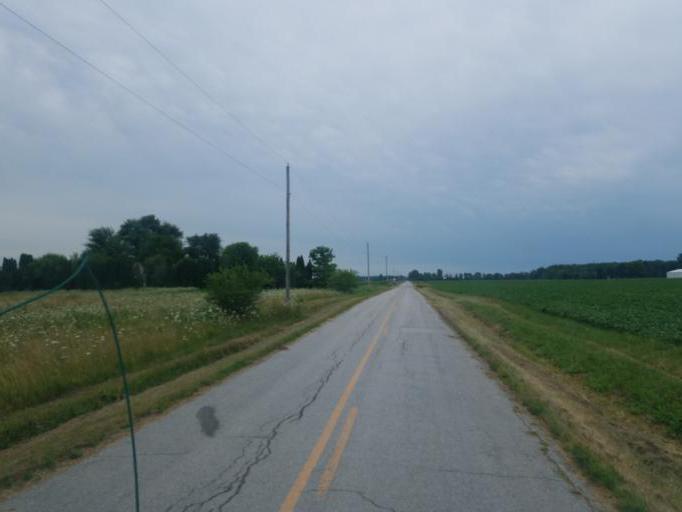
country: US
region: Ohio
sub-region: Defiance County
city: Hicksville
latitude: 41.2371
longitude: -84.8031
